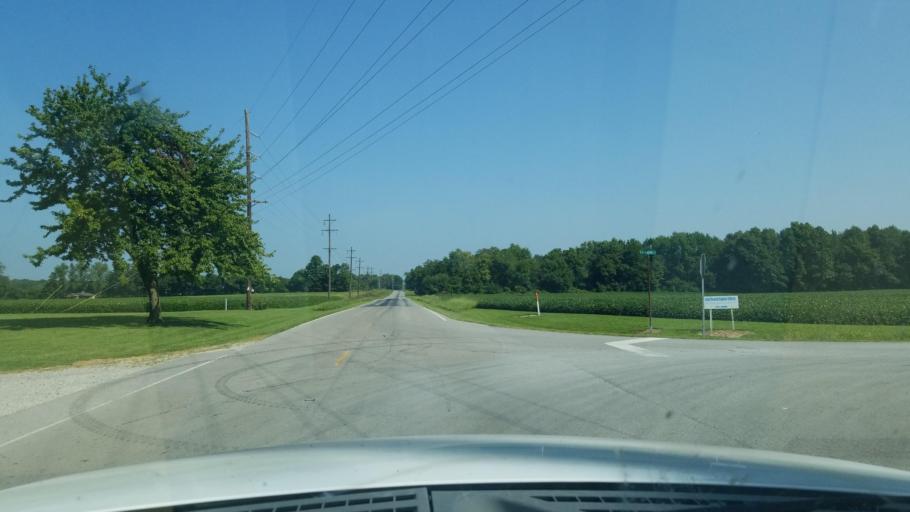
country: US
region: Illinois
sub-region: Saline County
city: Harrisburg
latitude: 37.8852
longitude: -88.6054
